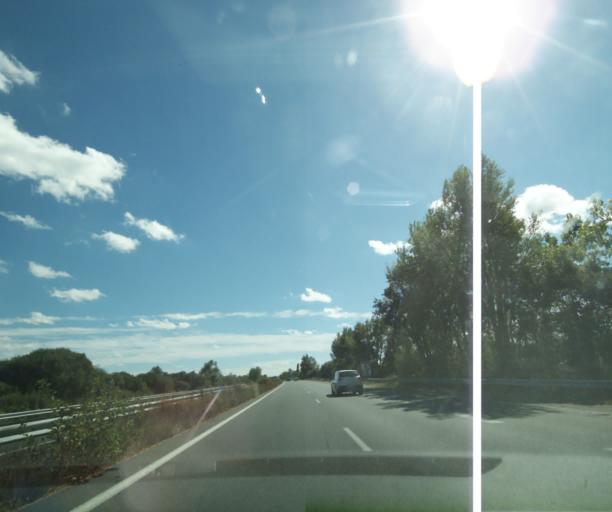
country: FR
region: Aquitaine
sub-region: Departement du Lot-et-Garonne
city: Damazan
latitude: 44.3398
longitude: 0.2522
